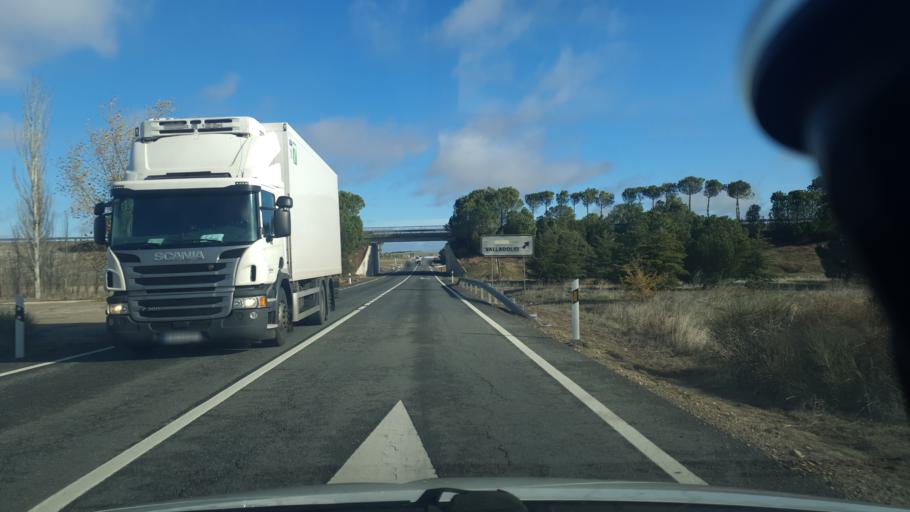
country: ES
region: Castille and Leon
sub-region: Provincia de Segovia
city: Codorniz
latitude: 41.0501
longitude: -4.6257
